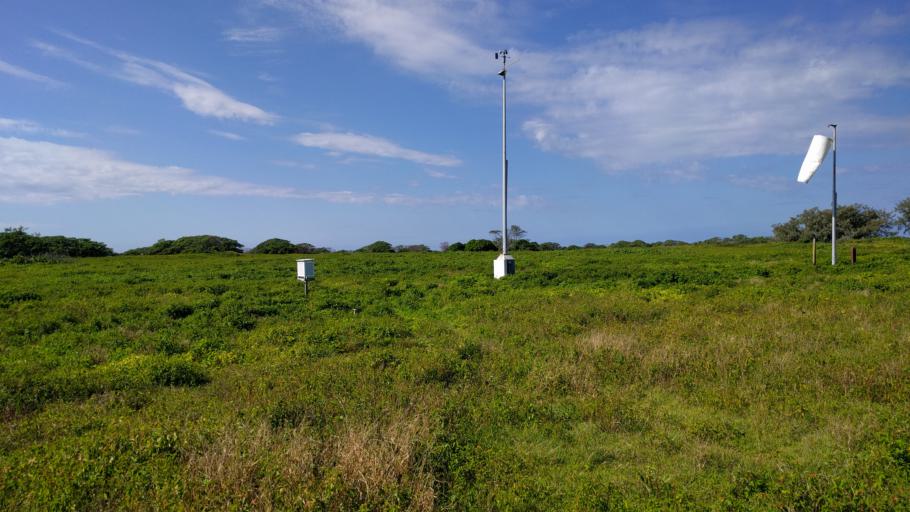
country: AU
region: Queensland
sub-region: Bundaberg
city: Bundaberg
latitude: -24.1115
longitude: 152.7159
